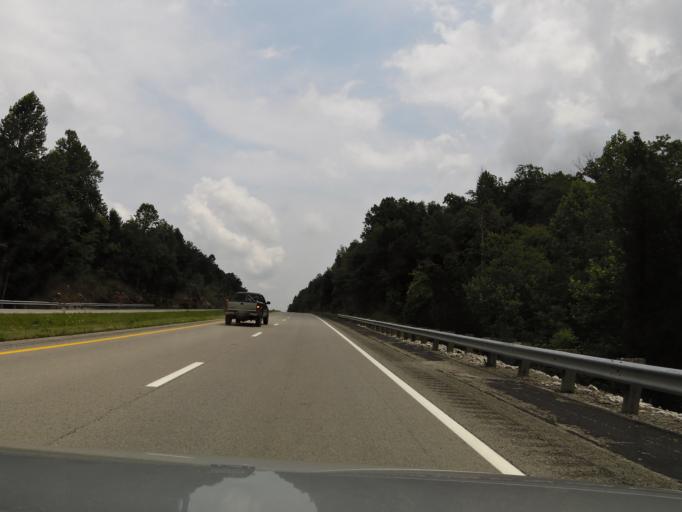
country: US
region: Kentucky
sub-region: Grayson County
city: Leitchfield
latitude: 37.5536
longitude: -86.0876
